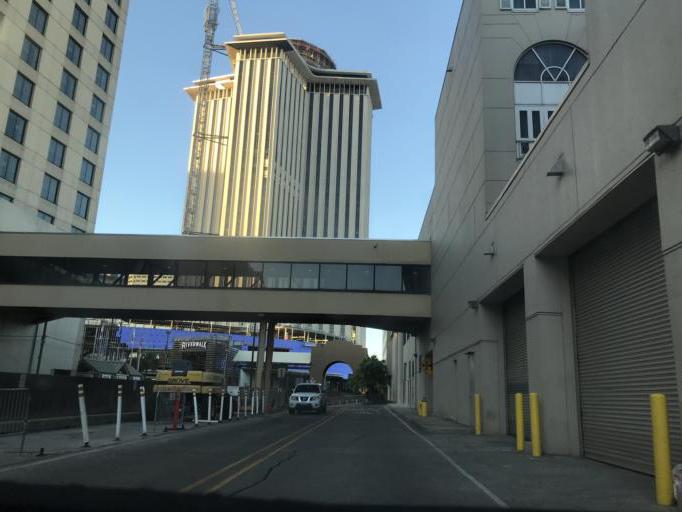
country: US
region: Louisiana
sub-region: Orleans Parish
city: New Orleans
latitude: 29.9474
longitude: -90.0629
